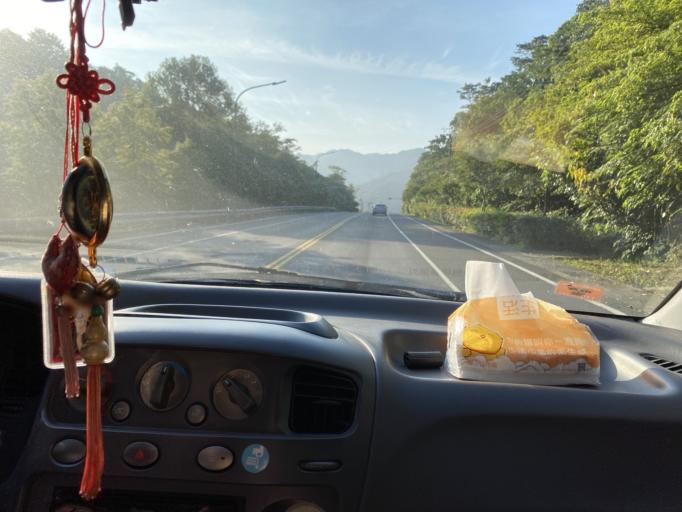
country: TW
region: Taiwan
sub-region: Keelung
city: Keelung
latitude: 25.0498
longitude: 121.7759
